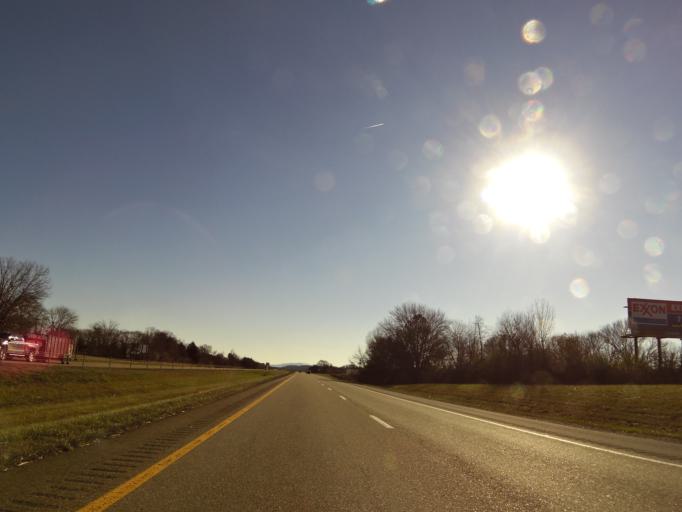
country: US
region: Tennessee
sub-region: Jefferson County
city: White Pine
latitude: 36.0338
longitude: -83.3234
